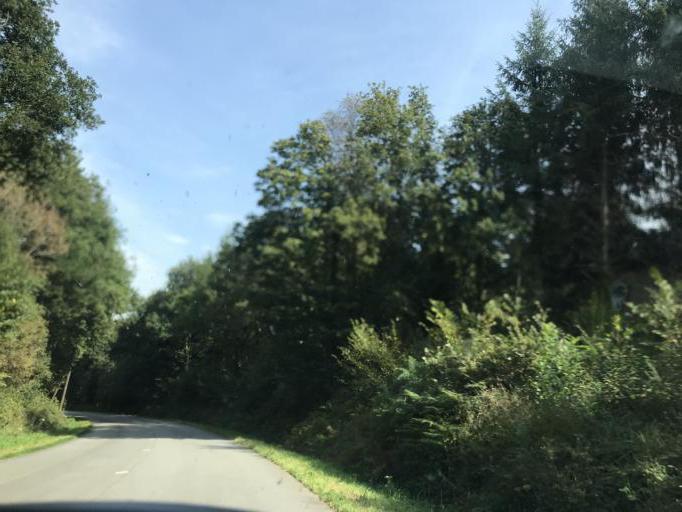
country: FR
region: Brittany
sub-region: Departement du Finistere
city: Loperec
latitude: 48.2945
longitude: -4.0411
